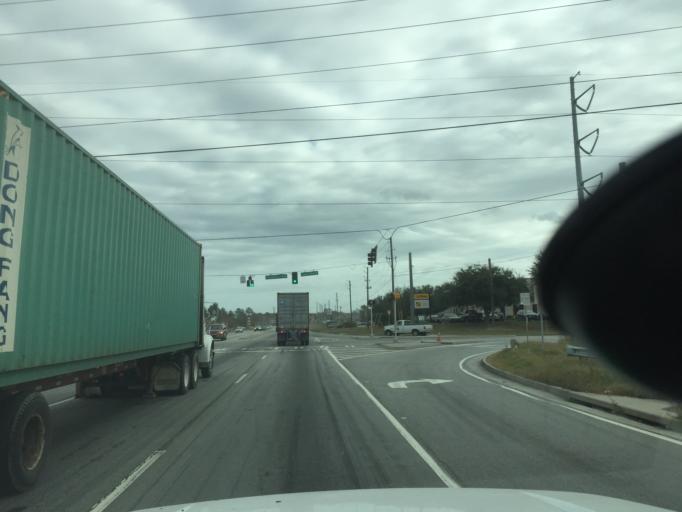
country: US
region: Georgia
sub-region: Chatham County
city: Garden City
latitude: 32.1264
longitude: -81.1759
